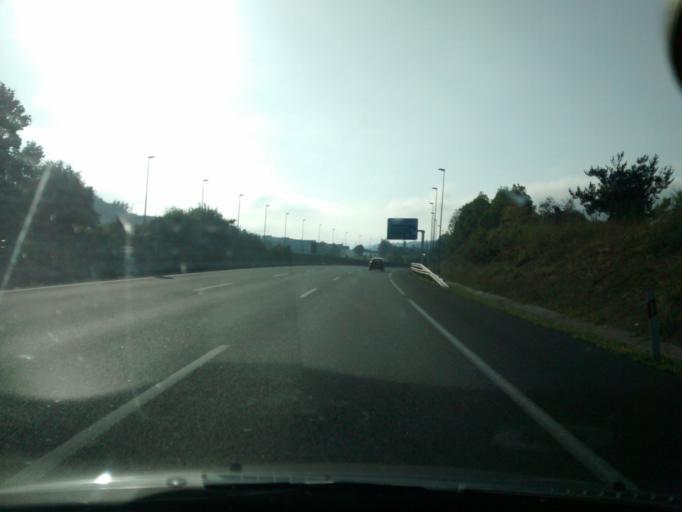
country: ES
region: Basque Country
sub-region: Bizkaia
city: Amorebieta
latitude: 43.2266
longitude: -2.7413
